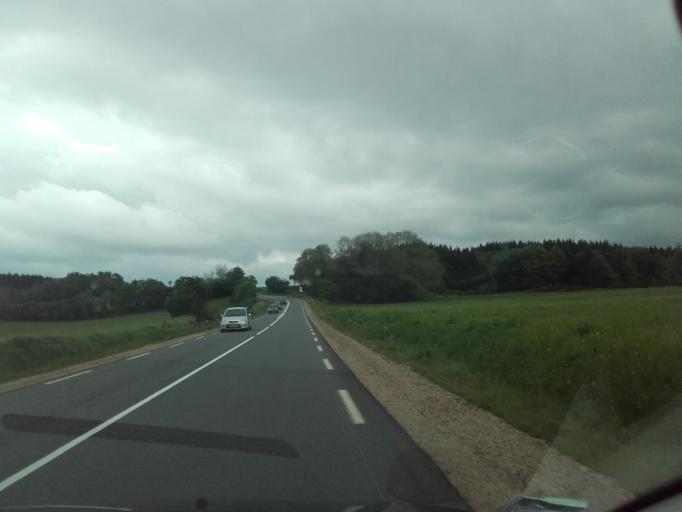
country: FR
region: Auvergne
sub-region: Departement du Puy-de-Dome
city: Saint-Ours
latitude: 45.8195
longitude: 2.9298
